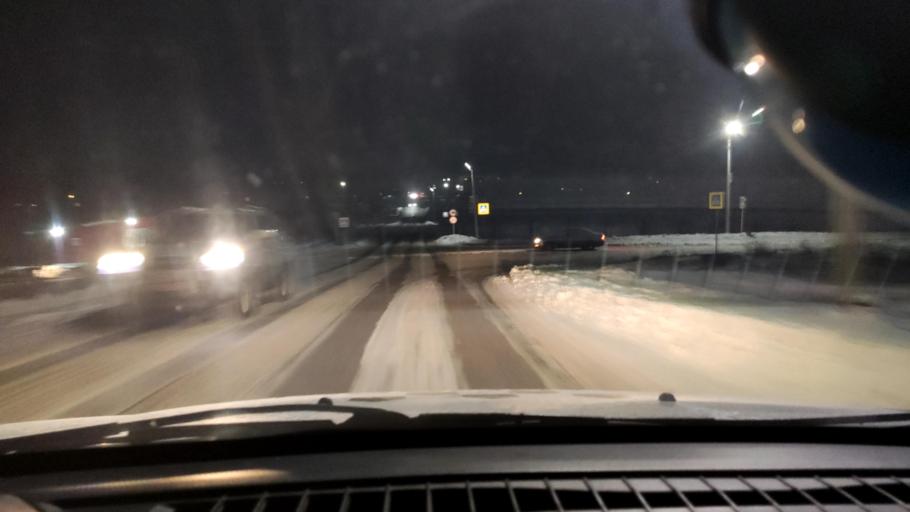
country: RU
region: Perm
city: Kultayevo
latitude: 57.9003
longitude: 55.9254
